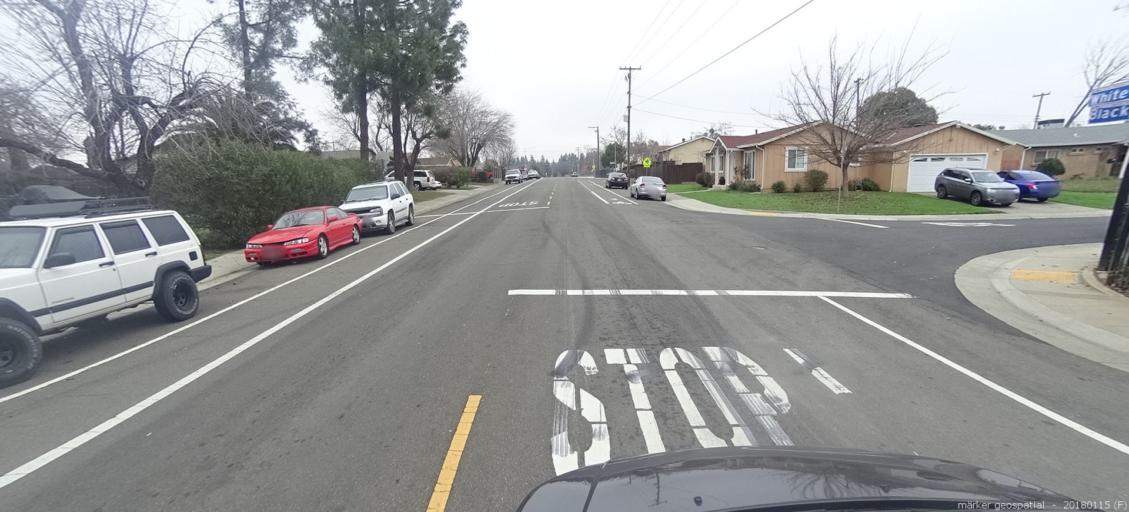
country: US
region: California
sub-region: Sacramento County
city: Rancho Cordova
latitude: 38.5857
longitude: -121.3027
